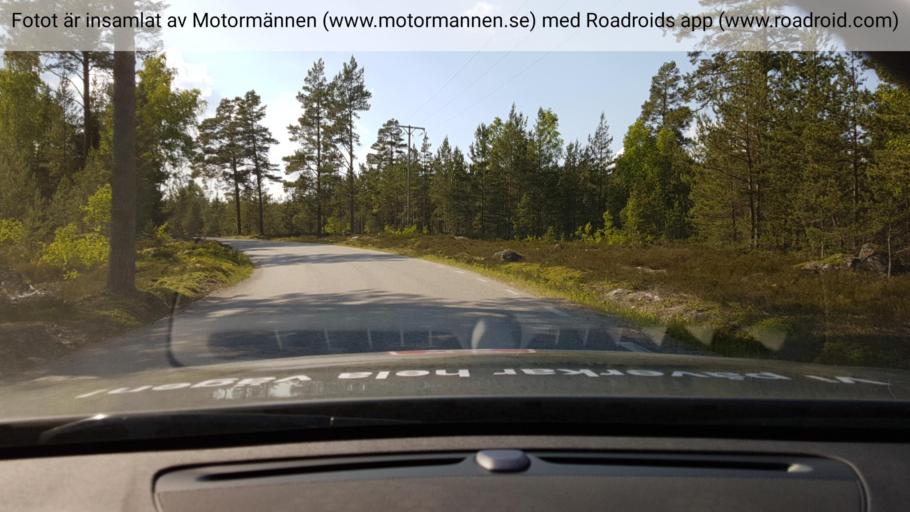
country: SE
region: Stockholm
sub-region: Varmdo Kommun
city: Mortnas
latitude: 59.2563
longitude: 18.4423
